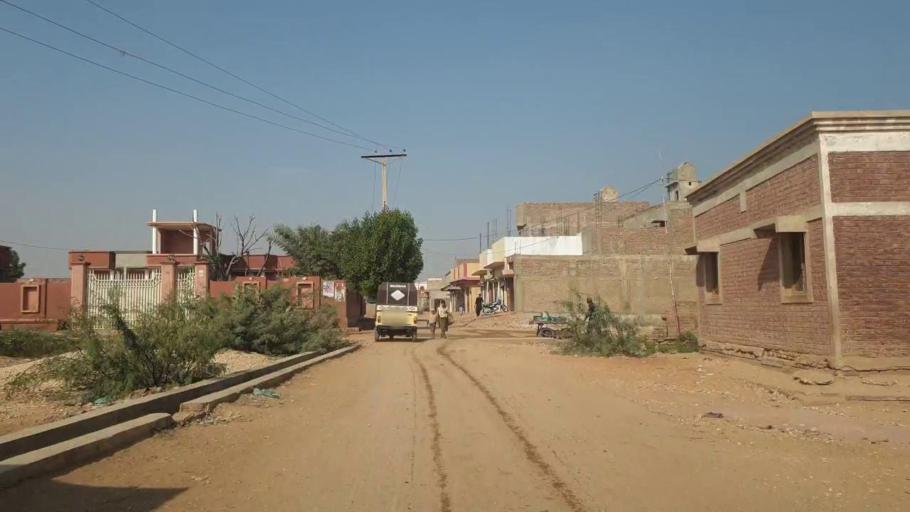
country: PK
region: Sindh
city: Jamshoro
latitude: 25.4405
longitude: 68.2813
